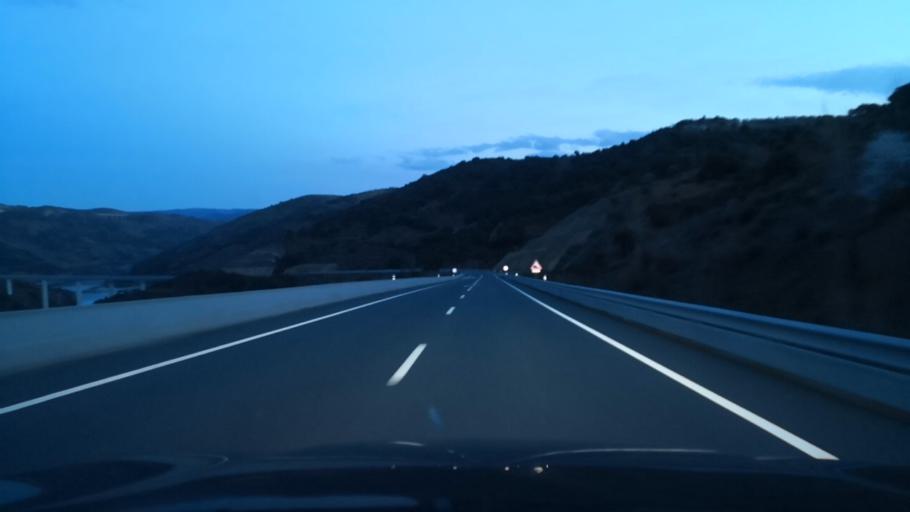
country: PT
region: Braganca
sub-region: Alfandega da Fe
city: Alfandega da Fe
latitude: 41.3154
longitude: -6.9281
